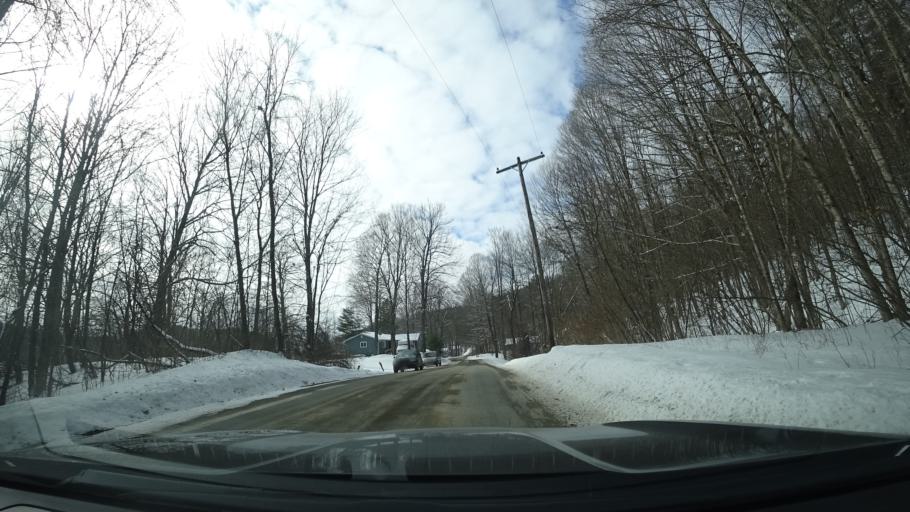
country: US
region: New York
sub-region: Washington County
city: Greenwich
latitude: 43.2175
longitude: -73.3561
